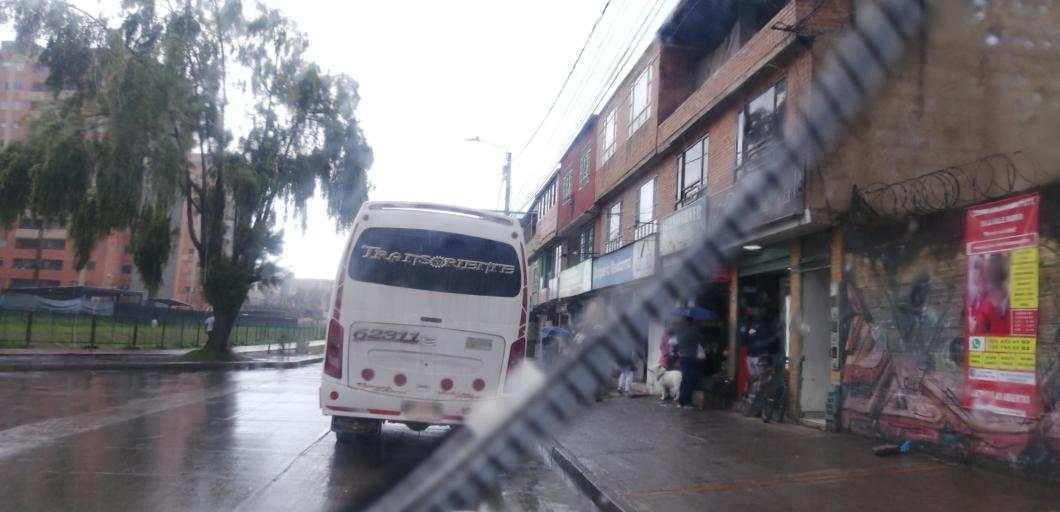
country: CO
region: Cundinamarca
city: Madrid
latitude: 4.7304
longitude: -74.2807
